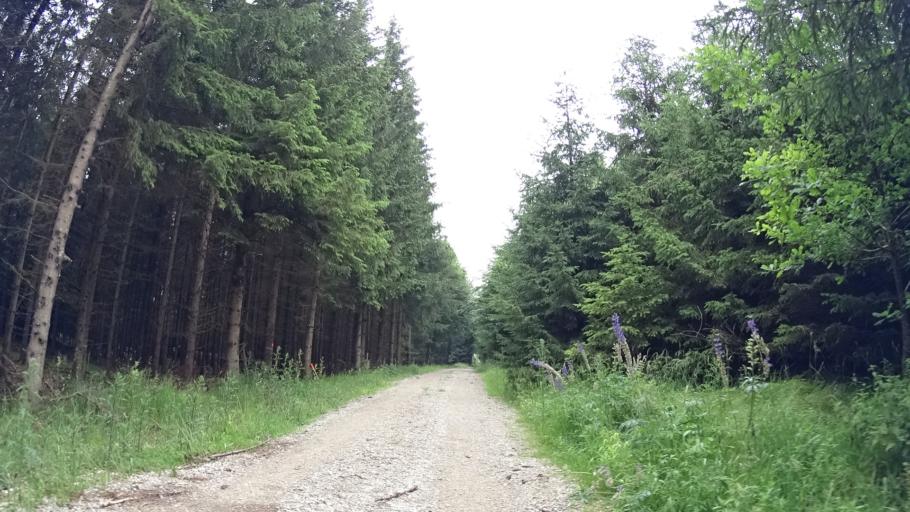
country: DE
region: Bavaria
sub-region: Upper Bavaria
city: Denkendorf
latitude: 48.8981
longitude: 11.4516
